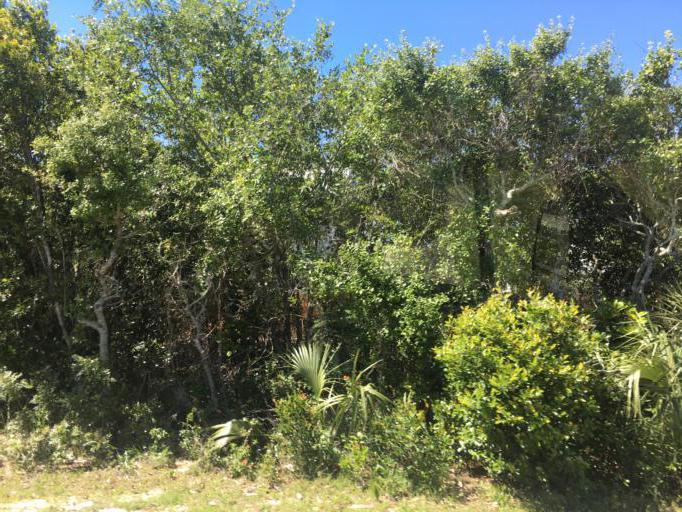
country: US
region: Florida
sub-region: Bay County
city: Panama City Beach
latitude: 30.2036
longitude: -85.8494
